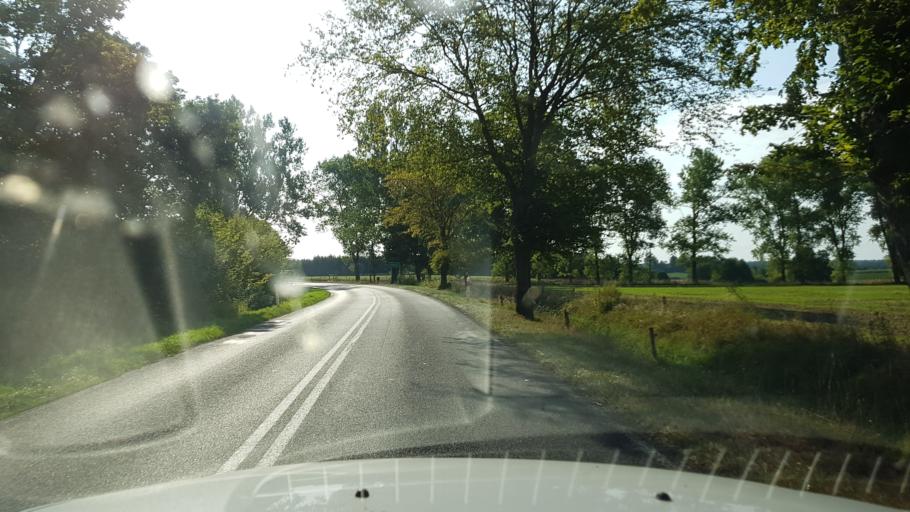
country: PL
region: West Pomeranian Voivodeship
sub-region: Powiat lobeski
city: Resko
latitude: 53.7771
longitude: 15.3649
